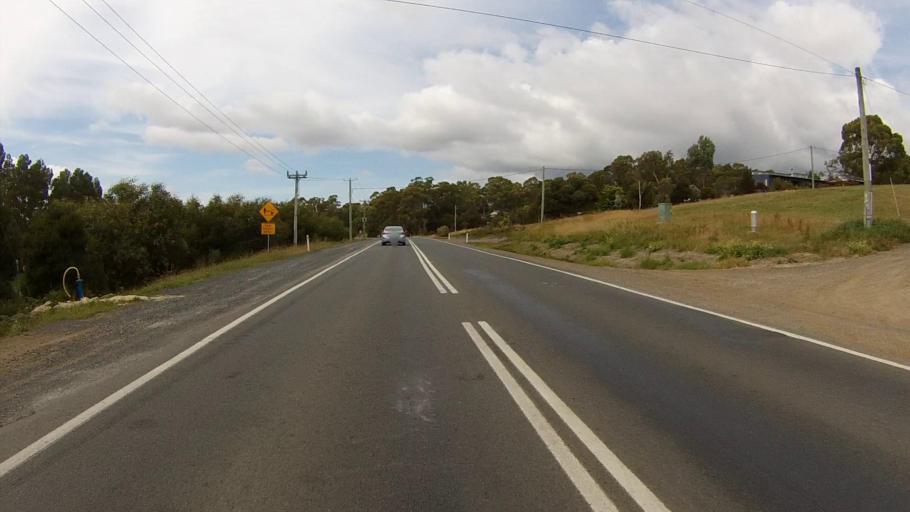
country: AU
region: Tasmania
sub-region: Kingborough
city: Margate
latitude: -43.0368
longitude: 147.2661
